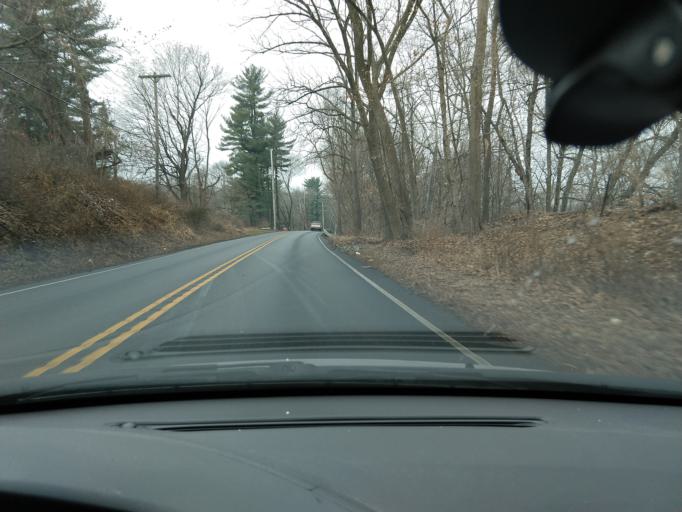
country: US
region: Pennsylvania
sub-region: Montgomery County
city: Stowe
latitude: 40.2353
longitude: -75.6862
